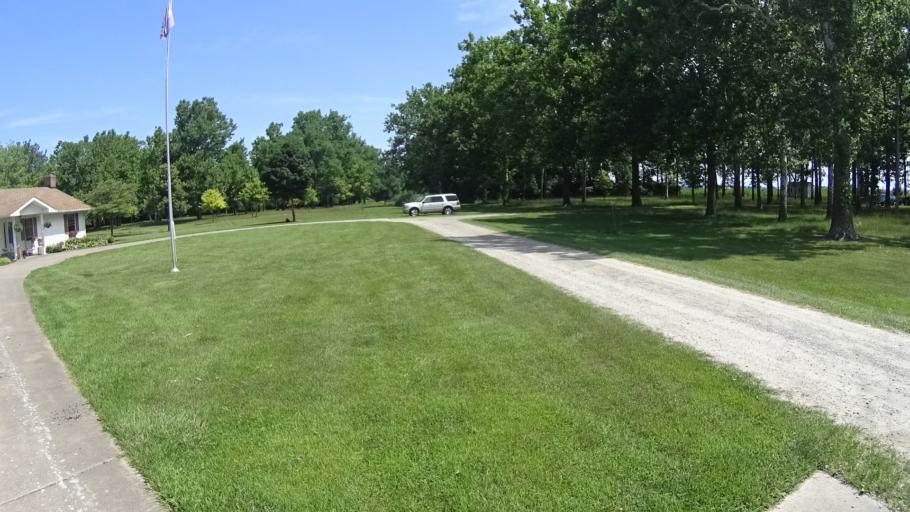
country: US
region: Ohio
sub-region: Erie County
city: Sandusky
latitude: 41.4074
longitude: -82.8028
